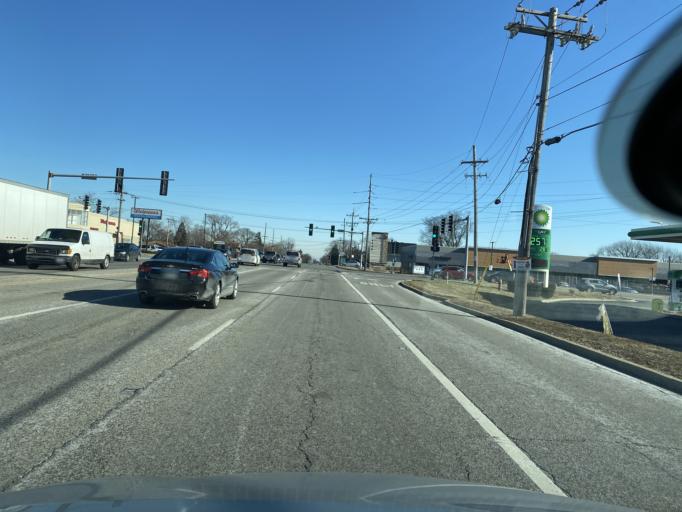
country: US
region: Illinois
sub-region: Cook County
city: Westchester
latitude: 41.8481
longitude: -87.9022
